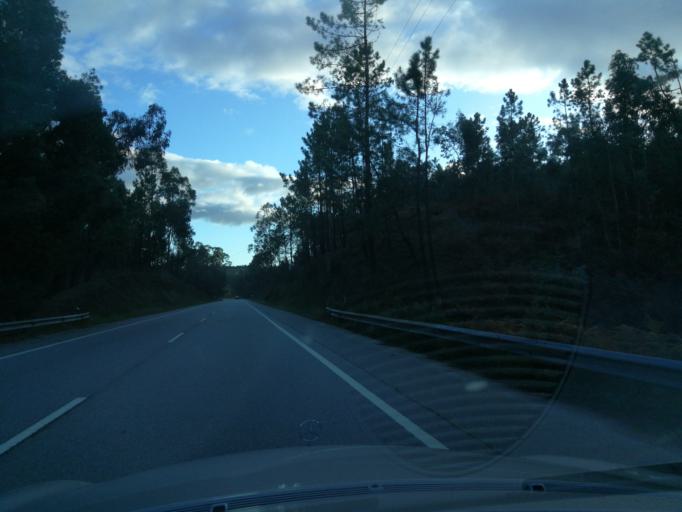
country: PT
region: Braga
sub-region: Barcelos
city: Vila Frescainha
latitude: 41.5506
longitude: -8.6522
